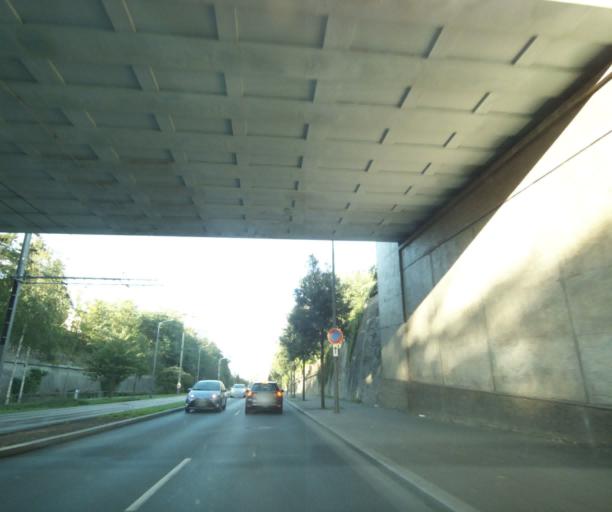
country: FR
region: Ile-de-France
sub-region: Departement des Hauts-de-Seine
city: Le Plessis-Robinson
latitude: 48.7962
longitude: 2.2759
